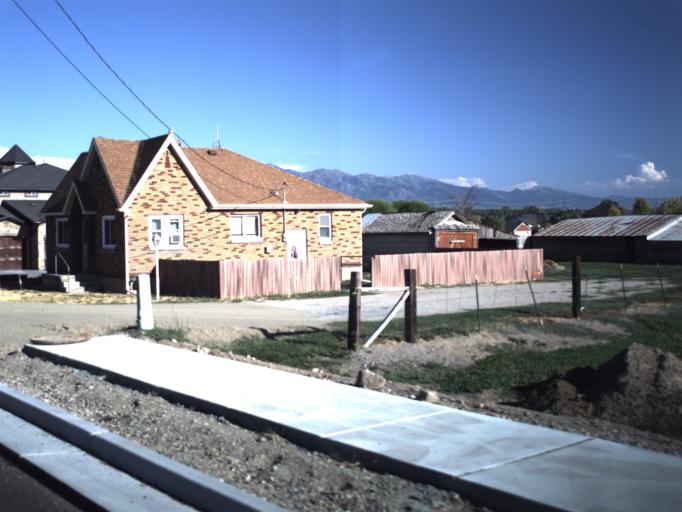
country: US
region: Utah
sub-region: Weber County
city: West Haven
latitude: 41.1907
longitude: -112.0711
